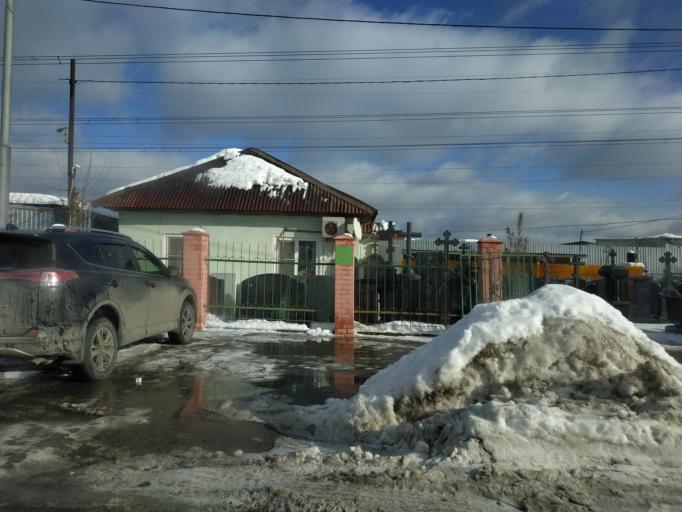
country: RU
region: Moskovskaya
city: Mosrentgen
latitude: 55.6092
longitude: 37.4481
